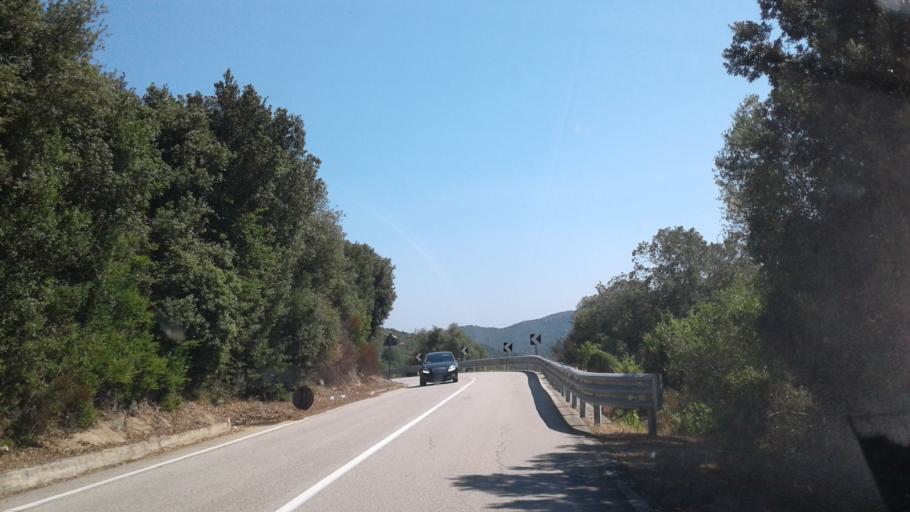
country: IT
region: Sardinia
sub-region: Provincia di Olbia-Tempio
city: Palau
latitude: 41.1301
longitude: 9.2945
